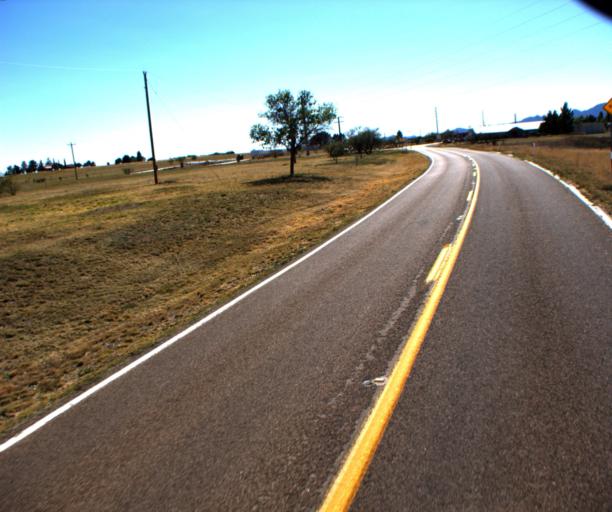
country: US
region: Arizona
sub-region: Pima County
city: Corona de Tucson
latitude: 31.6744
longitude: -110.6505
